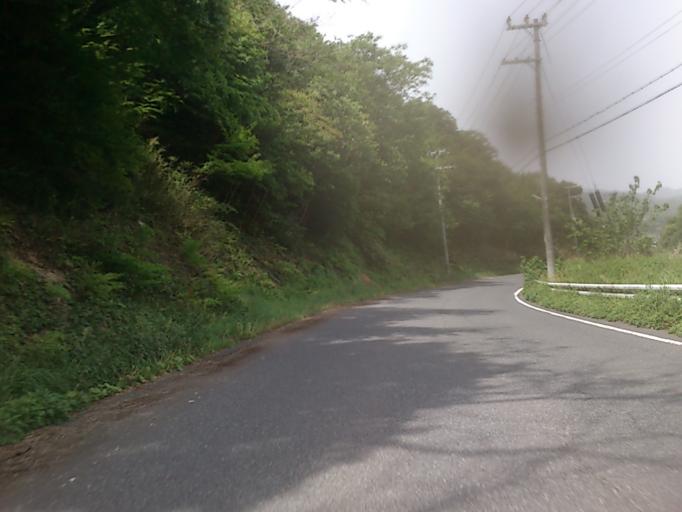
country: JP
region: Kyoto
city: Miyazu
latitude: 35.5738
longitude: 135.1080
